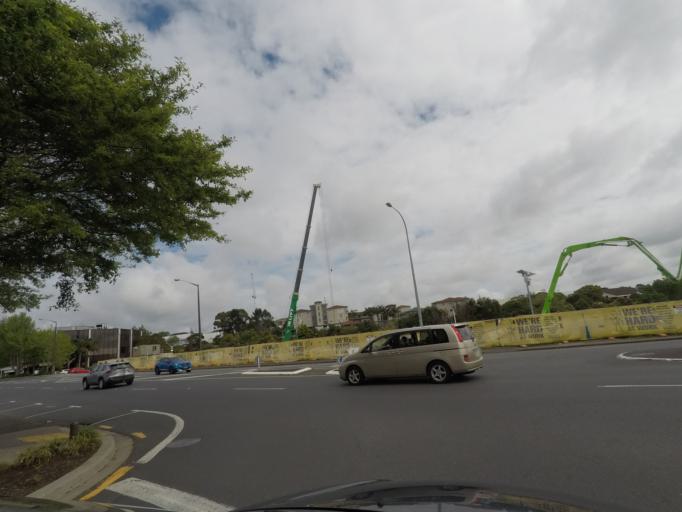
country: NZ
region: Auckland
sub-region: Auckland
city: Rosebank
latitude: -36.8777
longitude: 174.6326
